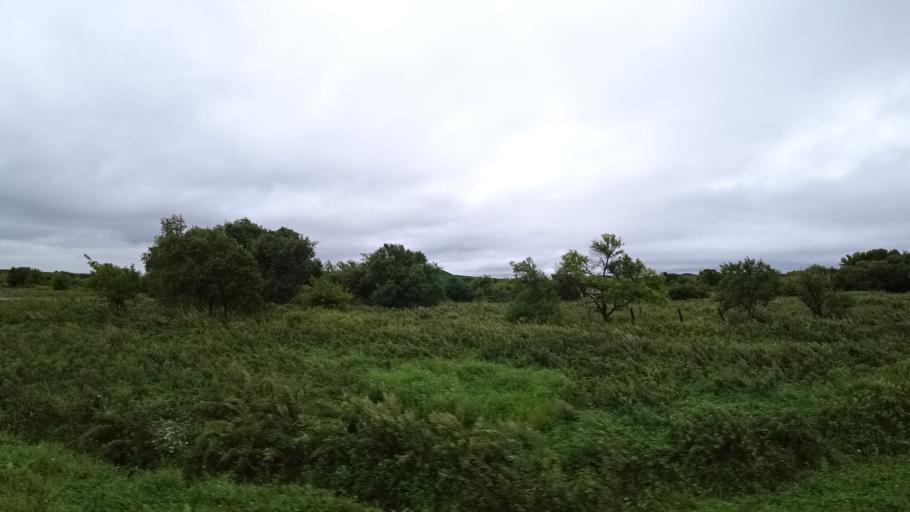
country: RU
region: Primorskiy
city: Monastyrishche
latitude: 44.2760
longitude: 132.4245
